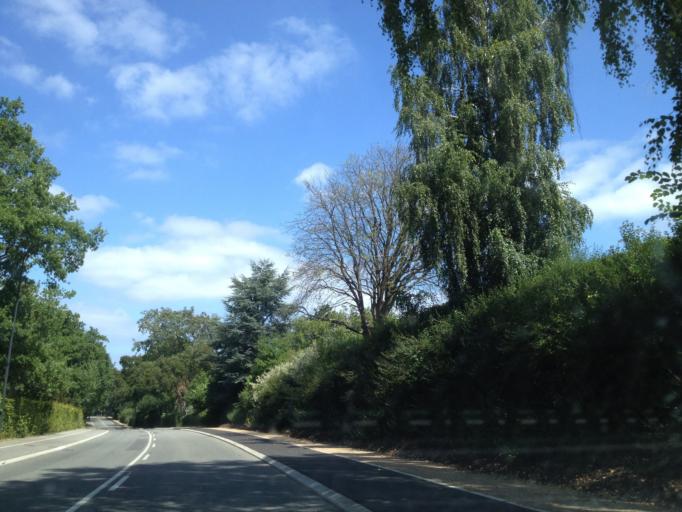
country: DK
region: Capital Region
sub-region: Rudersdal Kommune
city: Trorod
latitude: 55.8232
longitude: 12.5400
